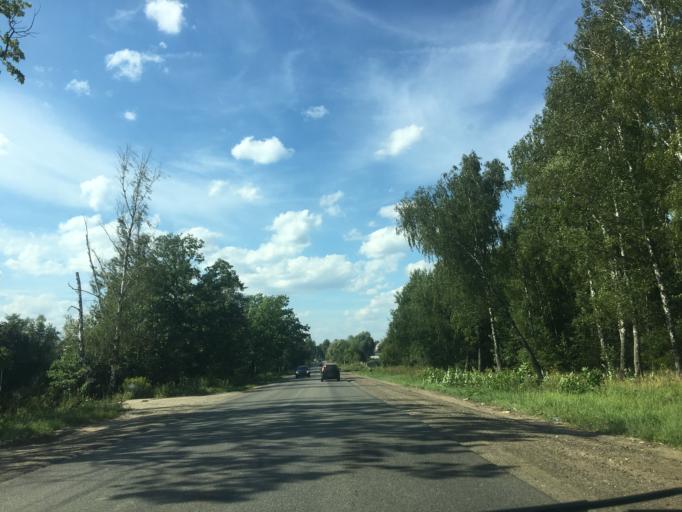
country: RU
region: Moskovskaya
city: Vidnoye
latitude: 55.5271
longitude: 37.6746
